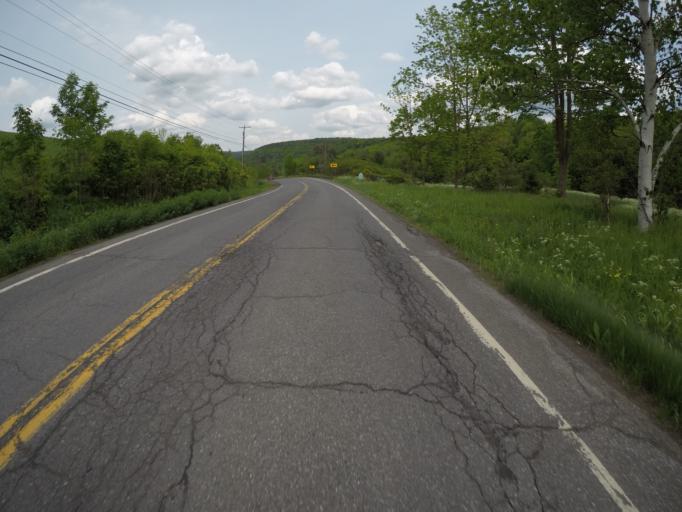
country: US
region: New York
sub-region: Delaware County
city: Stamford
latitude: 42.3576
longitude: -74.5055
